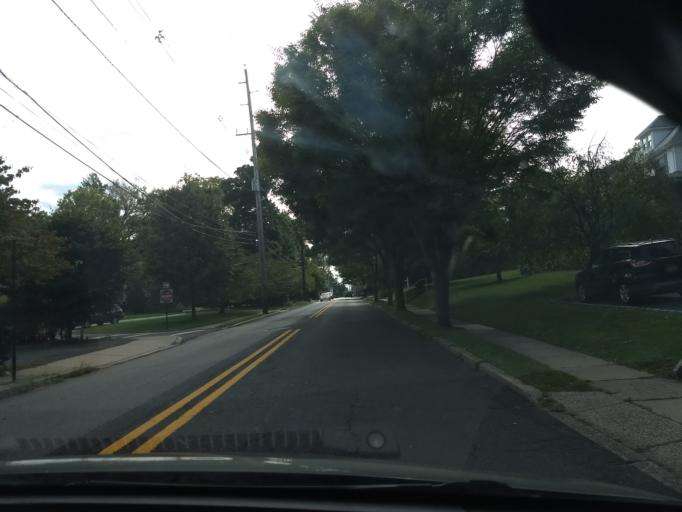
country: US
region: New Jersey
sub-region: Bergen County
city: Ridgewood
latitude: 40.9716
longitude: -74.1175
